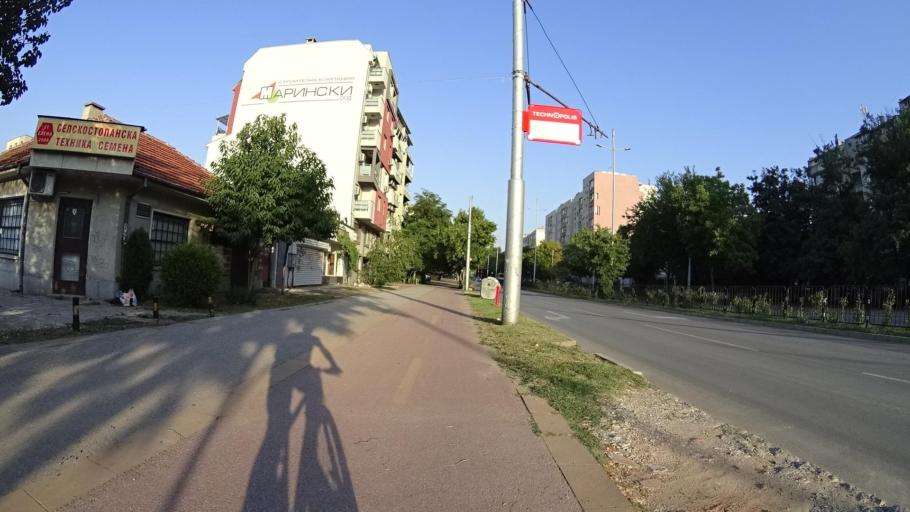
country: BG
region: Plovdiv
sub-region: Obshtina Plovdiv
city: Plovdiv
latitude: 42.1290
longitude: 24.7235
